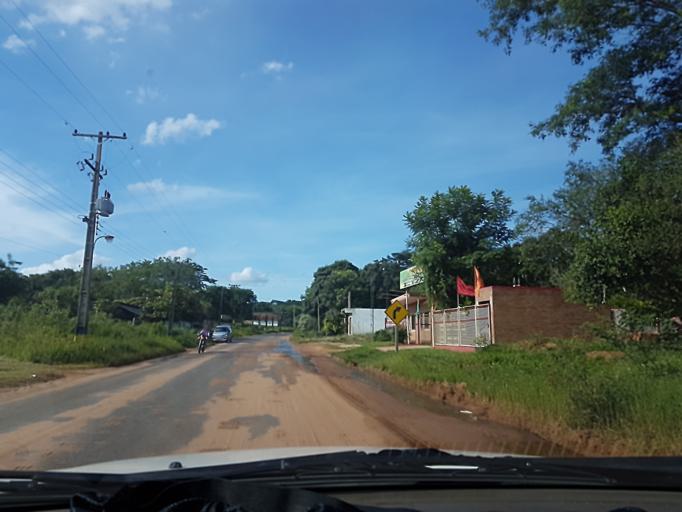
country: PY
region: Central
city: Limpio
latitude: -25.2260
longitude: -57.4492
